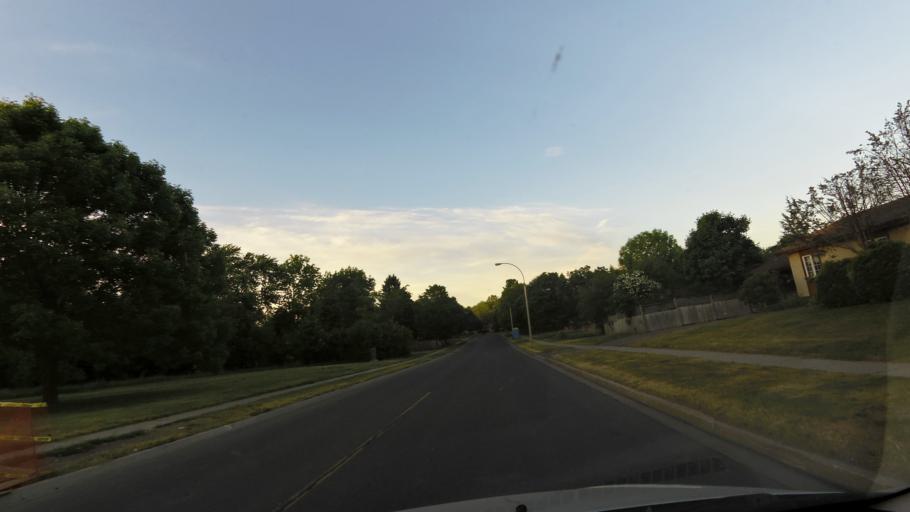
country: CA
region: Ontario
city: Peterborough
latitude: 44.3366
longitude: -78.3312
